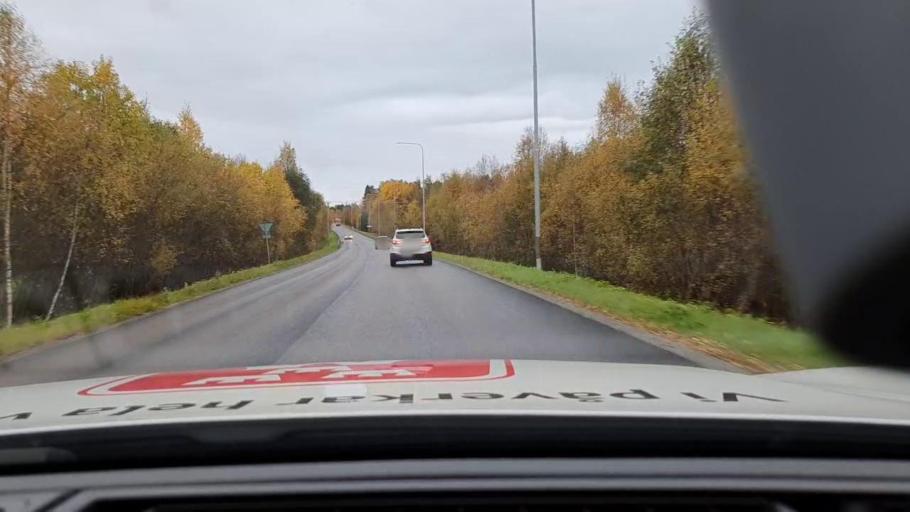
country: SE
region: Norrbotten
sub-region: Bodens Kommun
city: Saevast
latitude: 65.7673
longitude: 21.7396
